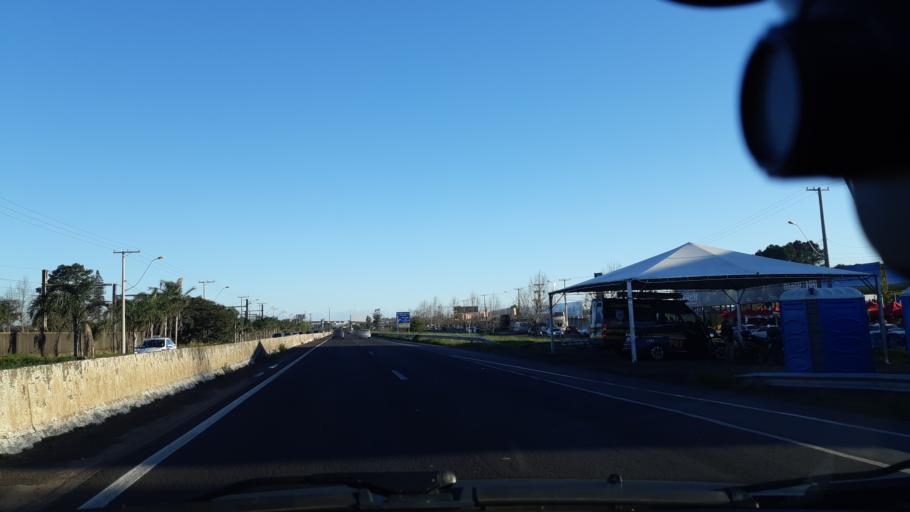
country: BR
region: Rio Grande do Sul
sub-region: Esteio
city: Esteio
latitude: -29.8541
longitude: -51.1801
